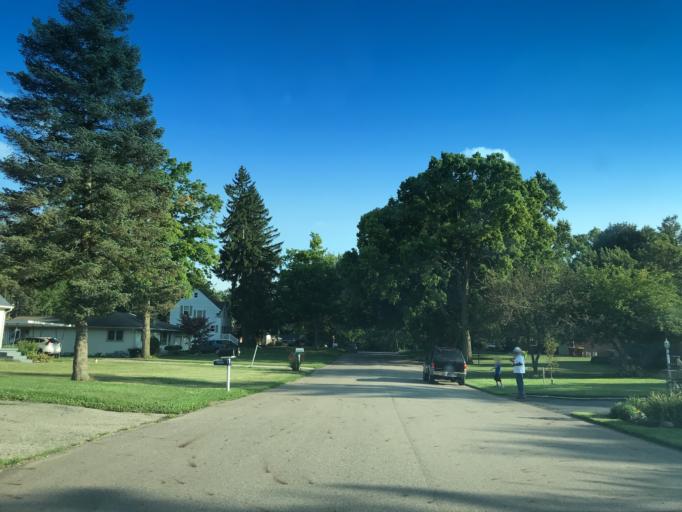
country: US
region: Michigan
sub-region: Eaton County
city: Waverly
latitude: 42.7087
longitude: -84.6088
